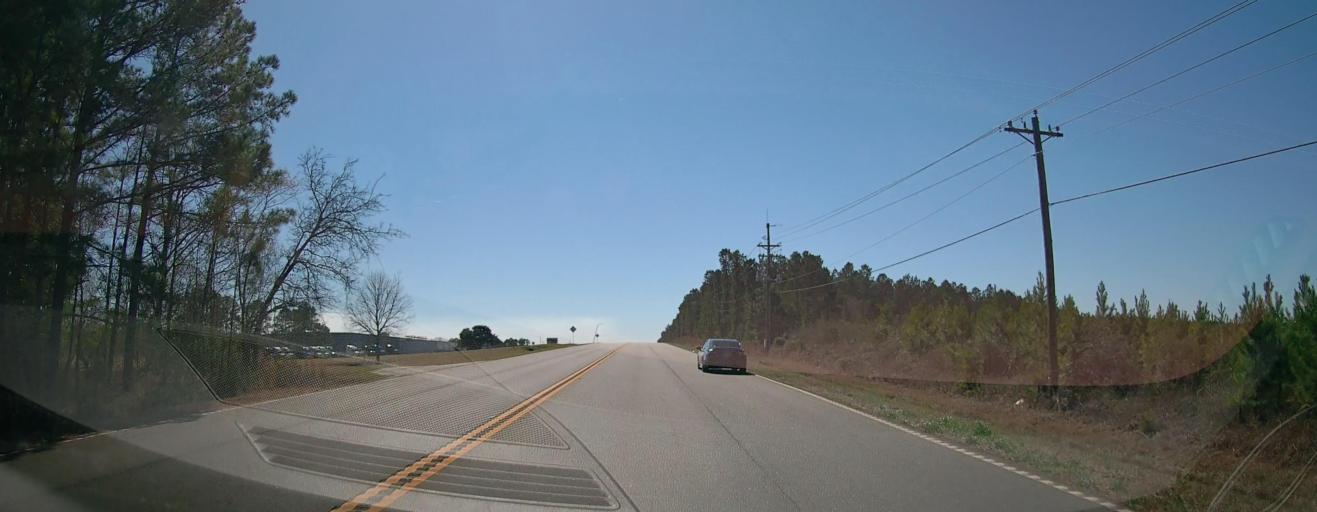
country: US
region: Georgia
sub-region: Houston County
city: Perry
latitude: 32.4473
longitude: -83.6283
